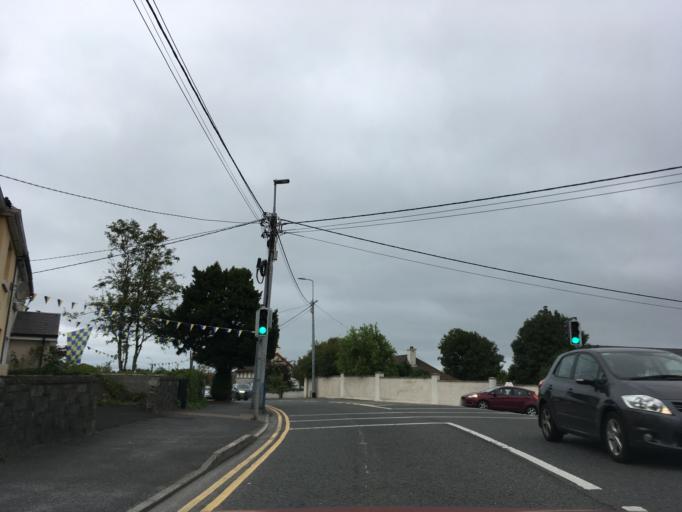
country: IE
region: Munster
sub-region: An Clar
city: Ennis
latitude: 52.8382
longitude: -8.9794
